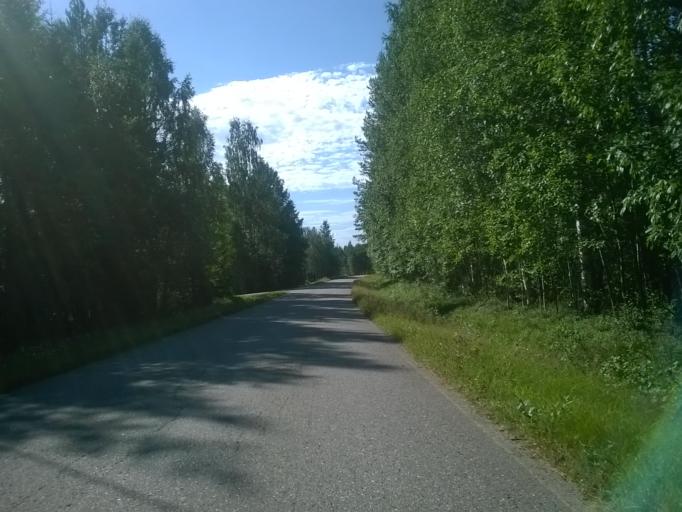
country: FI
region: Kainuu
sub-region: Kehys-Kainuu
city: Kuhmo
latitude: 64.1341
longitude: 29.4063
